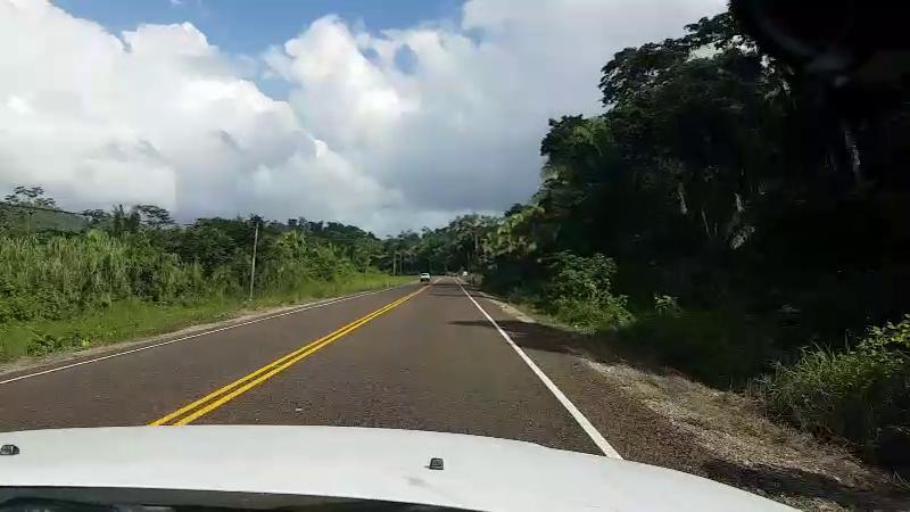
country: BZ
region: Cayo
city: Belmopan
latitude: 17.1486
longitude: -88.7220
